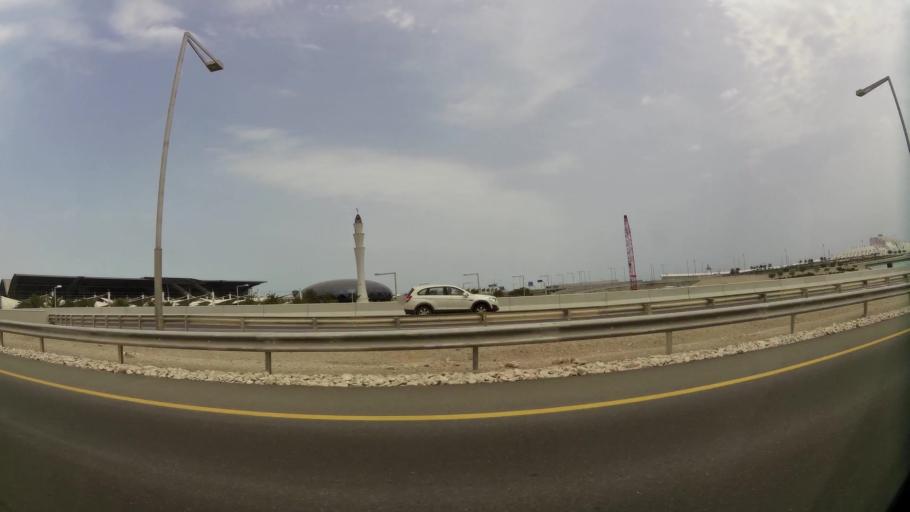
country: QA
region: Al Wakrah
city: Al Wakrah
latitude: 25.2563
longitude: 51.6140
